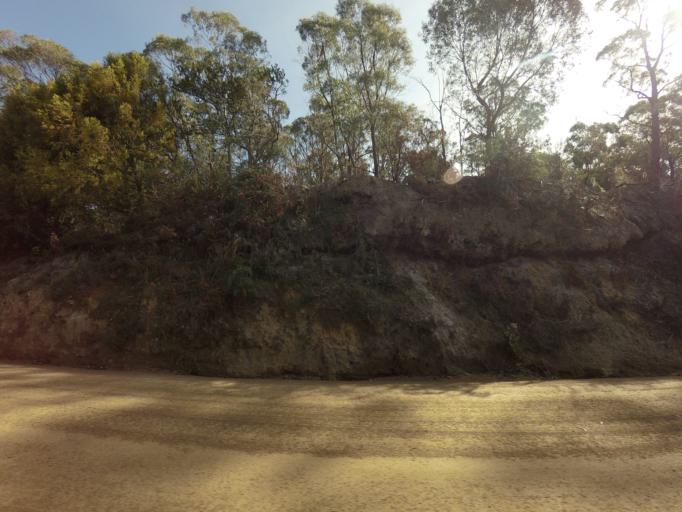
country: AU
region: Tasmania
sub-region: Kingborough
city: Kettering
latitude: -43.0794
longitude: 147.2648
